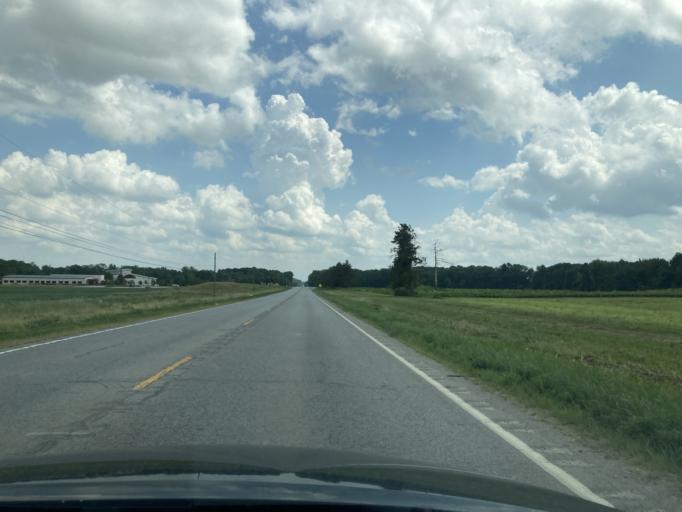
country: US
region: Indiana
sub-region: Boone County
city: Zionsville
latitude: 39.9895
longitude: -86.2604
